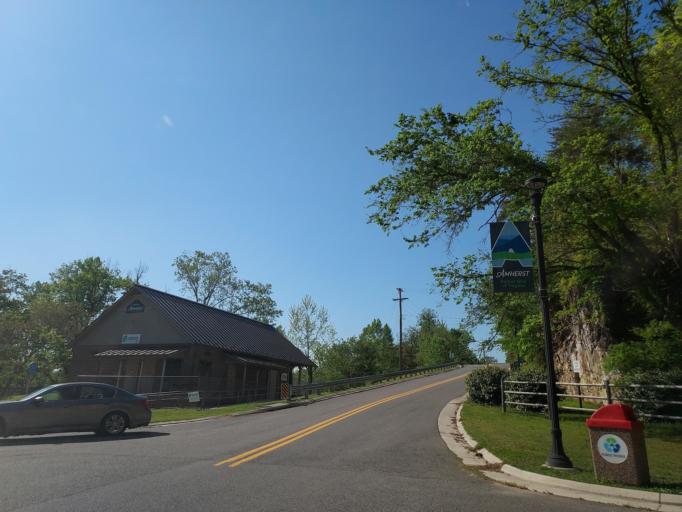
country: US
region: Virginia
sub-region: City of Lynchburg
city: Lynchburg
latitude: 37.4170
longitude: -79.1369
